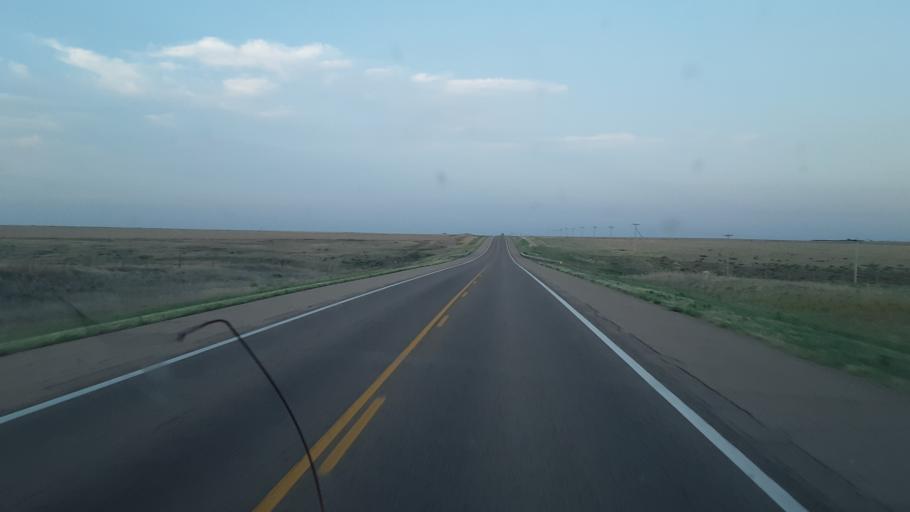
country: US
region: Kansas
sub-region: Kearny County
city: Lakin
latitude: 37.9440
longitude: -101.4387
